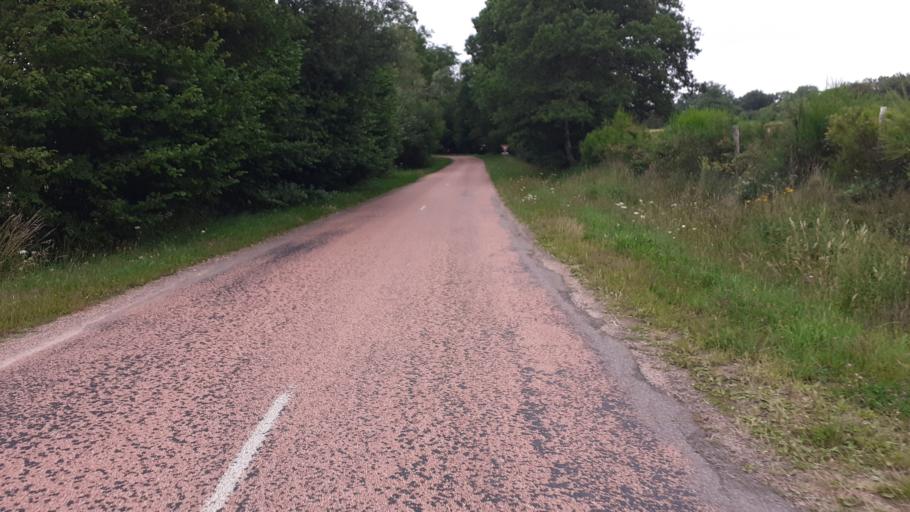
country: FR
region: Bourgogne
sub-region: Departement de la Cote-d'Or
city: Saulieu
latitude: 47.2815
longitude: 4.1423
